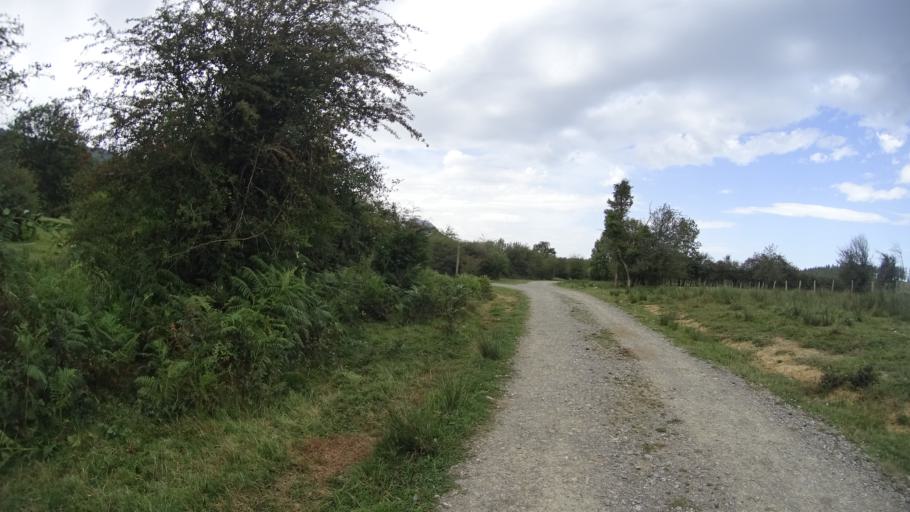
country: ES
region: Basque Country
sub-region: Bizkaia
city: Zeanuri
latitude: 43.0497
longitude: -2.7206
